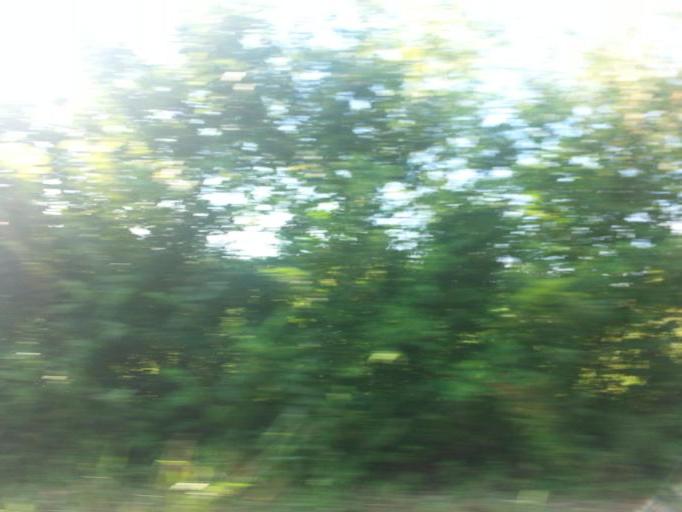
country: US
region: Tennessee
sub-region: Blount County
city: Eagleton Village
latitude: 35.8280
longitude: -83.9555
